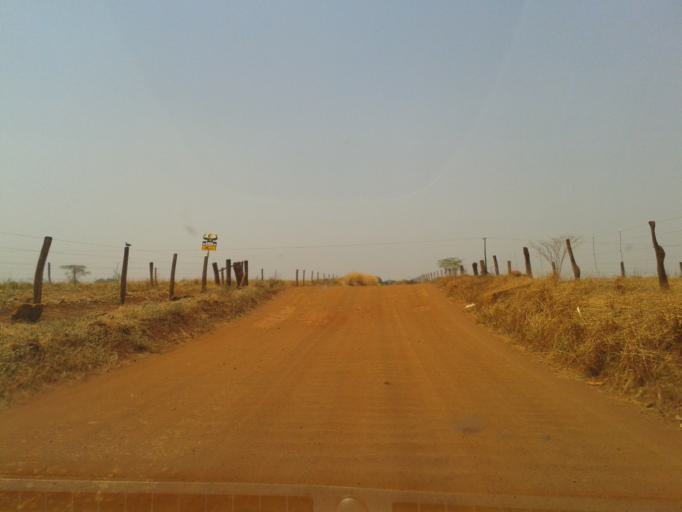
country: BR
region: Minas Gerais
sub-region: Centralina
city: Centralina
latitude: -18.7163
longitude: -49.2144
